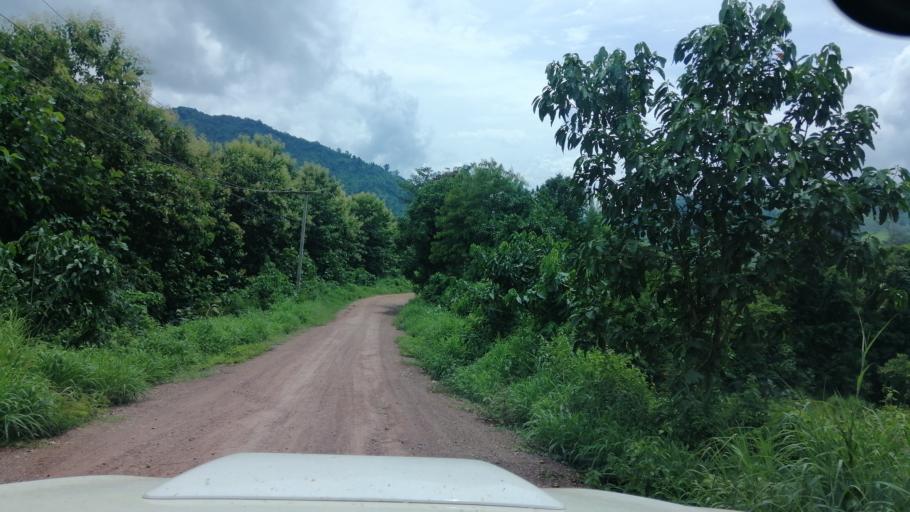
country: TH
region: Nan
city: Bo Kluea
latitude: 18.8993
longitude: 101.4643
